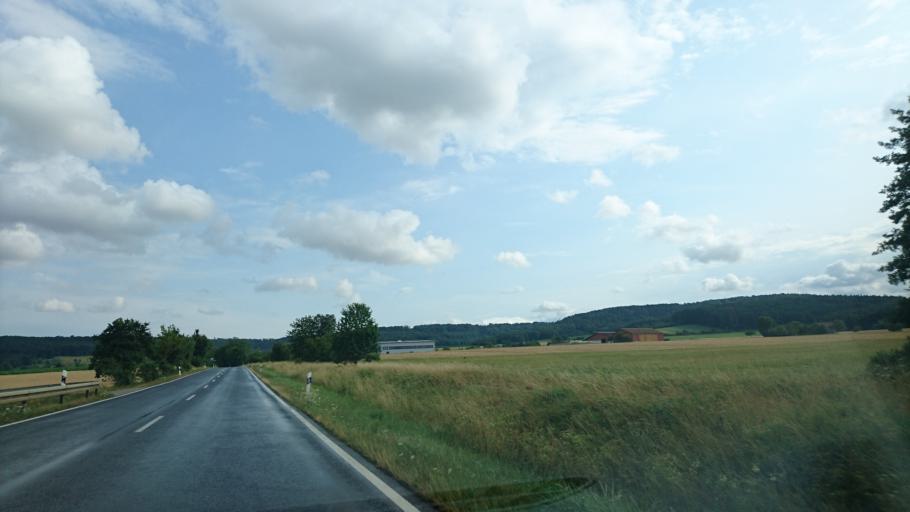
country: DE
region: Bavaria
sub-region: Regierungsbezirk Mittelfranken
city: Thalmassing
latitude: 49.0973
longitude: 11.2095
